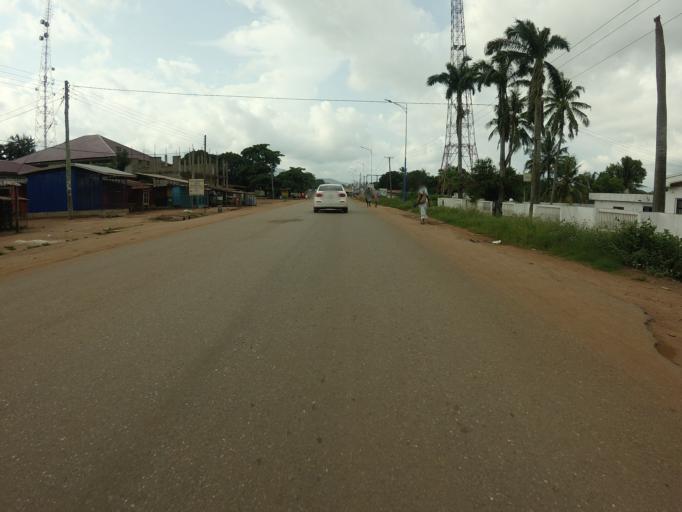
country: GH
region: Volta
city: Hohoe
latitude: 7.1449
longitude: 0.4652
